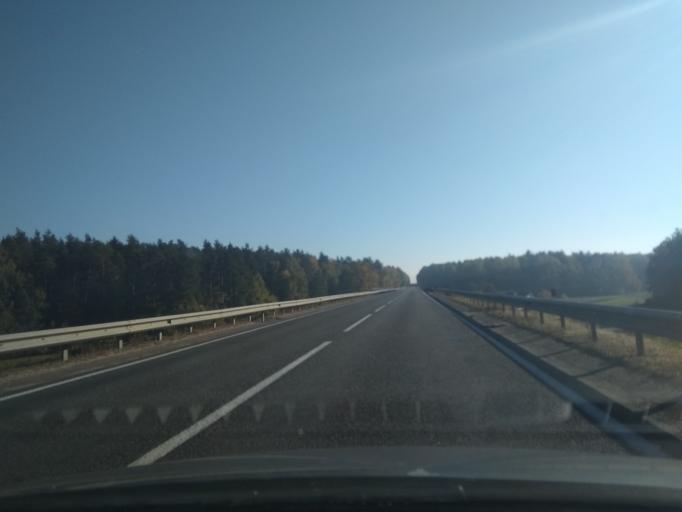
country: BY
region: Grodnenskaya
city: Zel'va
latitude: 53.1392
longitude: 24.9216
